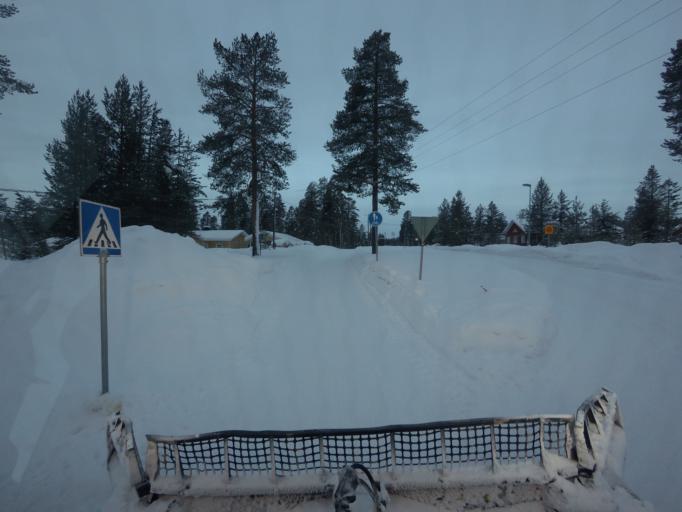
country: FI
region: Lapland
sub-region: Tunturi-Lappi
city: Kolari
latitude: 67.6232
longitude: 24.1541
